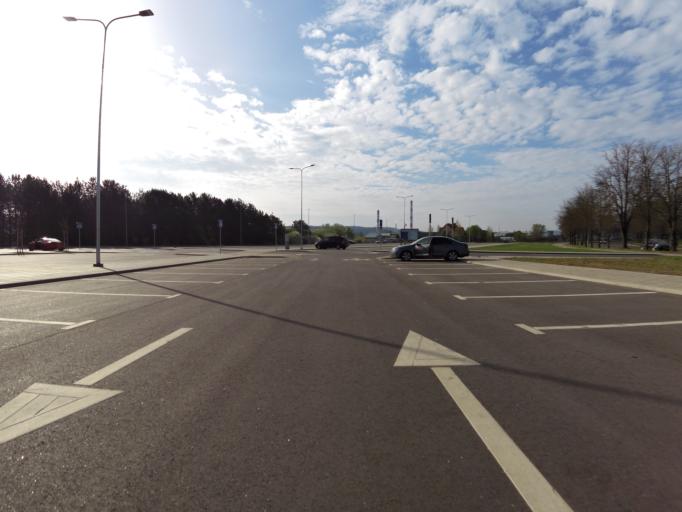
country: LT
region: Vilnius County
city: Vilkpede
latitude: 54.6755
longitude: 25.2276
